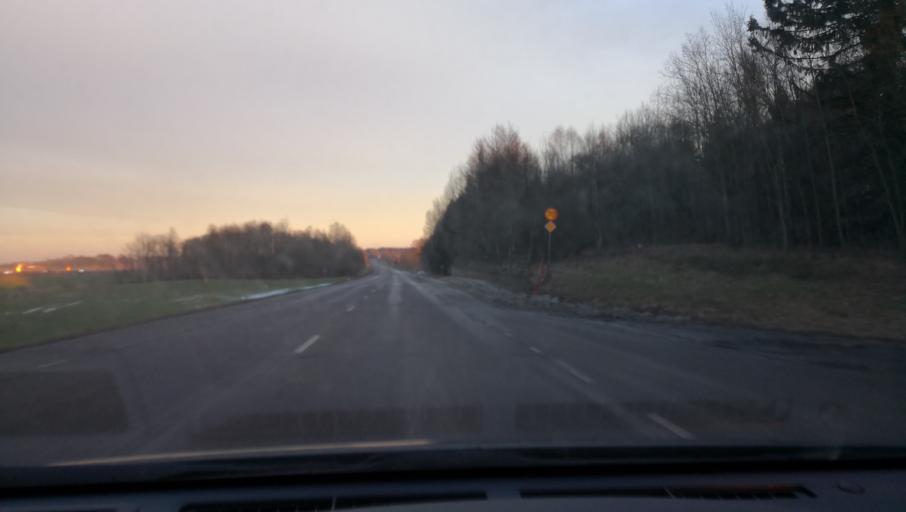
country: SE
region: OErebro
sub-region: Orebro Kommun
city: Vintrosa
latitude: 59.2429
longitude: 14.9969
